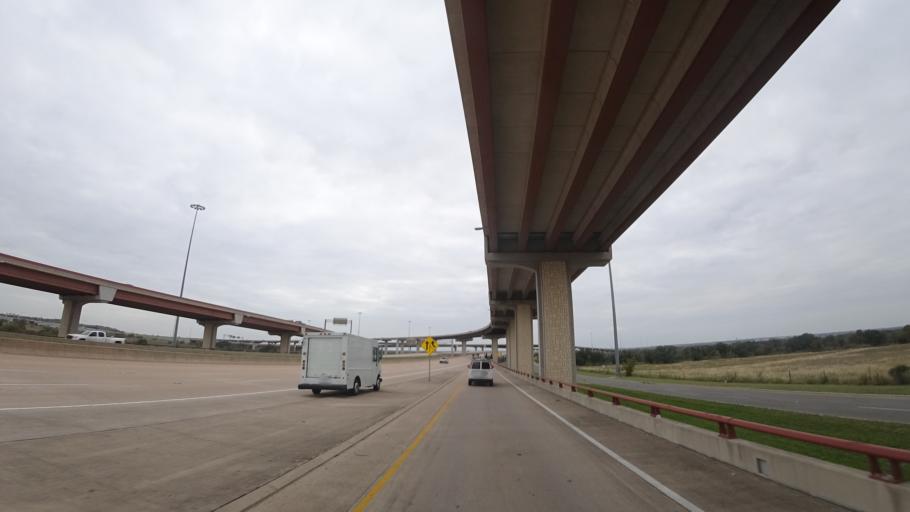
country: US
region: Texas
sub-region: Williamson County
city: Round Rock
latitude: 30.4774
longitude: -97.6982
